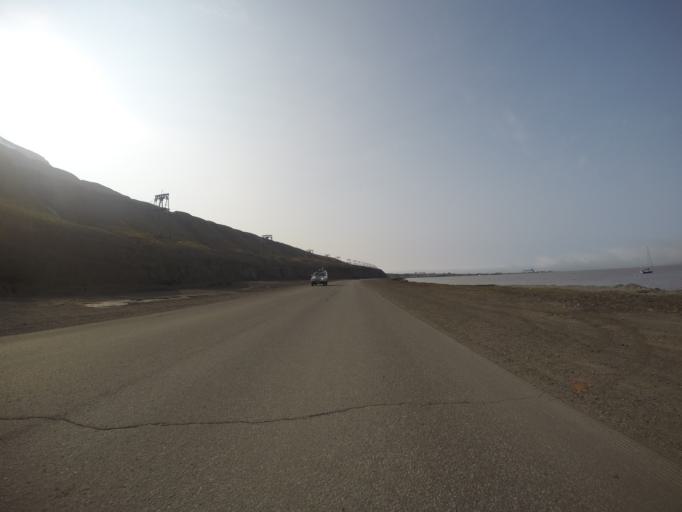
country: SJ
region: Svalbard
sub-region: Spitsbergen
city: Longyearbyen
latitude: 78.2291
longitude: 15.5921
